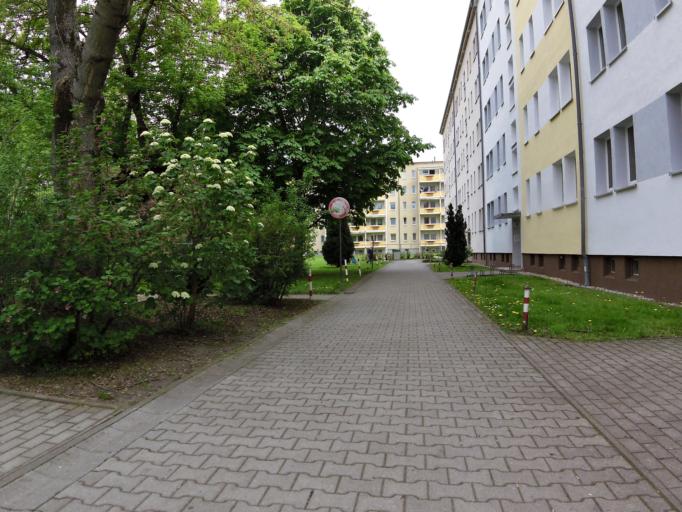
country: DE
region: Saxony
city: Markkleeberg
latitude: 51.3054
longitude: 12.3847
